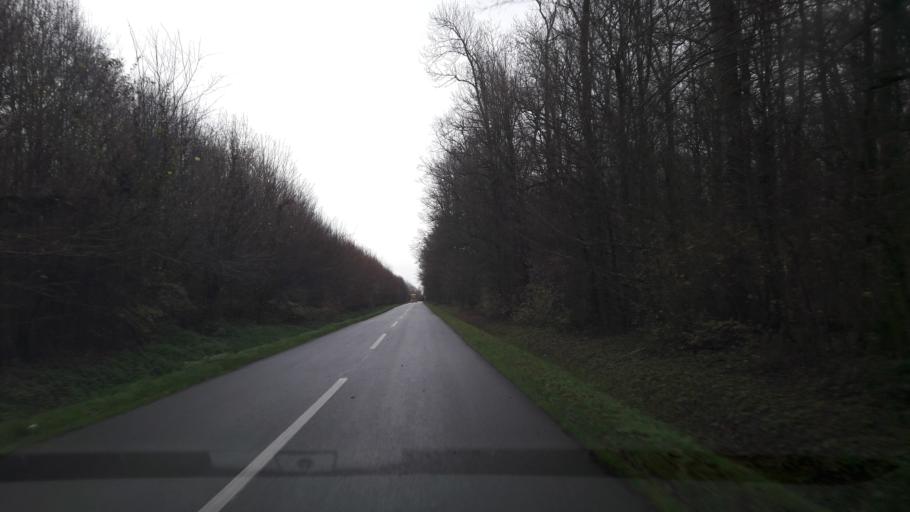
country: HR
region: Osjecko-Baranjska
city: Velimirovac
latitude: 45.6294
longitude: 18.0981
